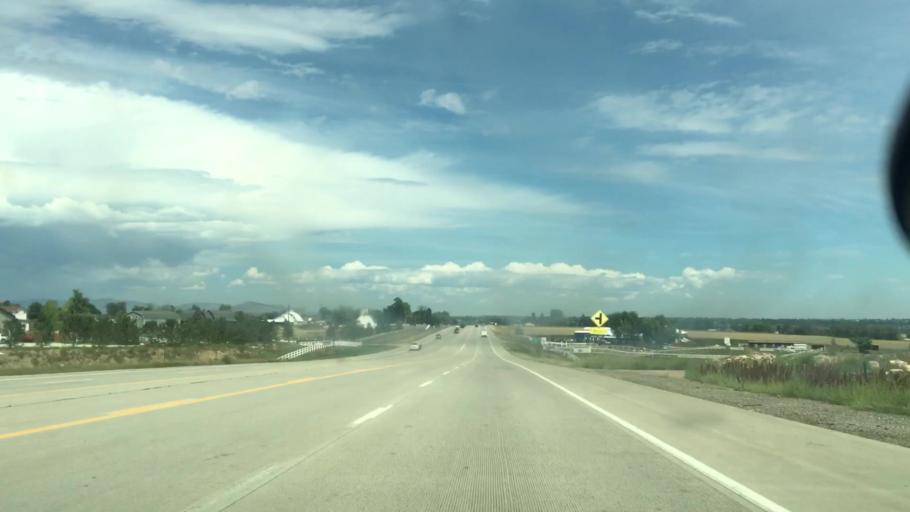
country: US
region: Colorado
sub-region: Larimer County
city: Berthoud
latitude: 40.2606
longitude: -105.1025
